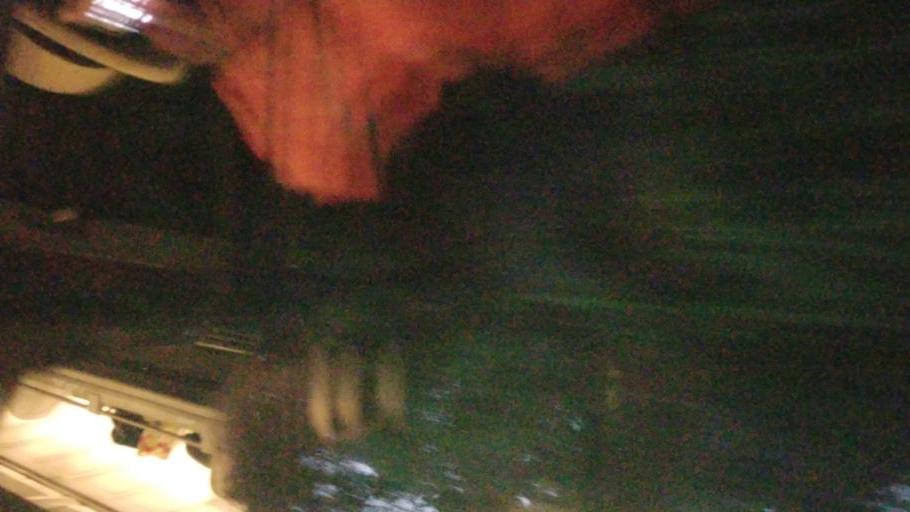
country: US
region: Virginia
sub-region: Greene County
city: Ruckersville
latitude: 38.1553
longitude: -78.3503
